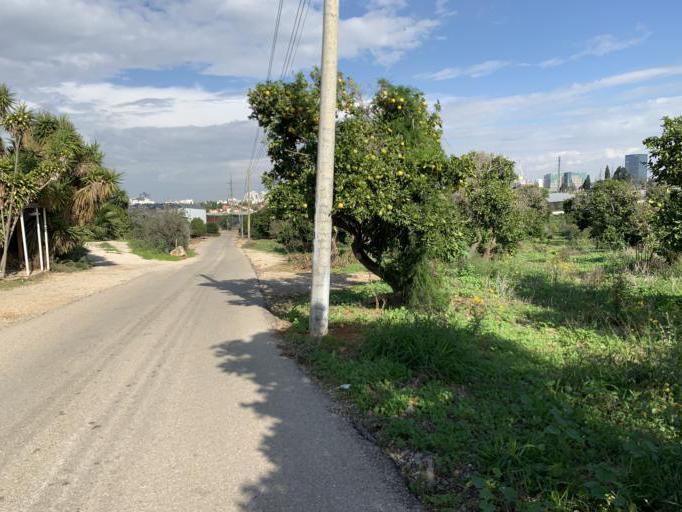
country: IL
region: Central District
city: Ra'anana
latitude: 32.1681
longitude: 34.8772
